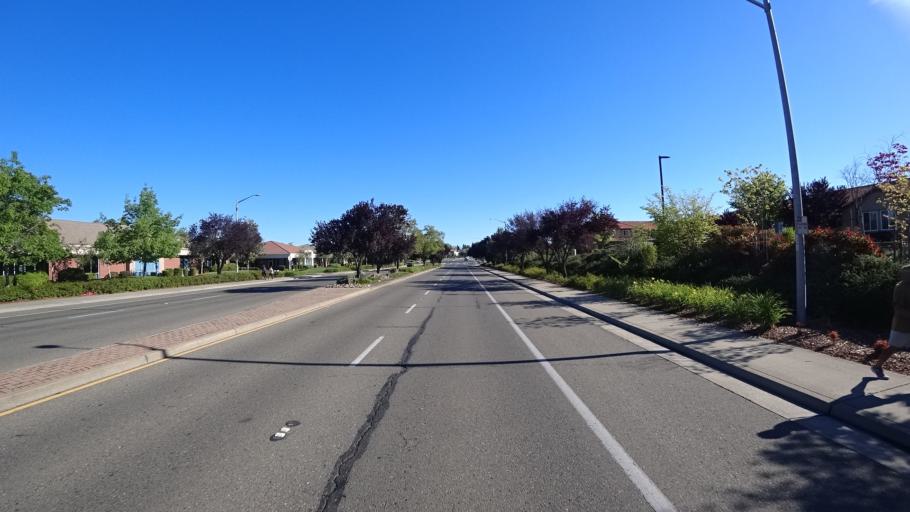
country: US
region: California
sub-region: Placer County
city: Rocklin
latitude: 38.8122
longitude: -121.2584
